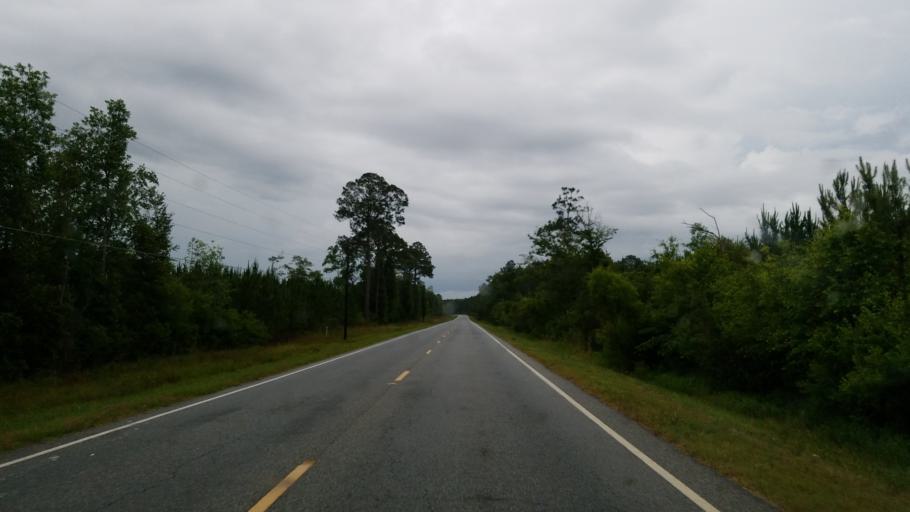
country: US
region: Georgia
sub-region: Berrien County
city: Ray City
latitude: 31.0572
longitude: -83.1487
